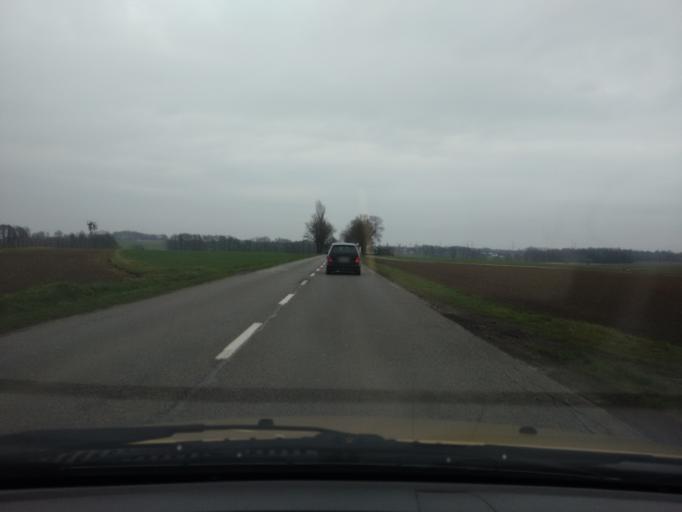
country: PL
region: Silesian Voivodeship
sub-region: Powiat pszczynski
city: Radostowice
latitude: 49.9850
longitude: 18.8500
